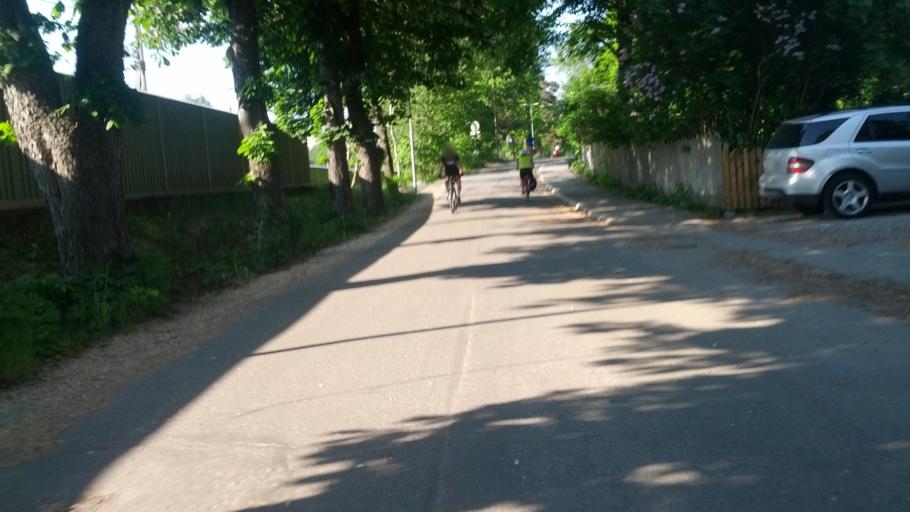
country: SE
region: Stockholm
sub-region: Norrtalje Kommun
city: Bergshamra
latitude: 59.3893
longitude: 18.0457
